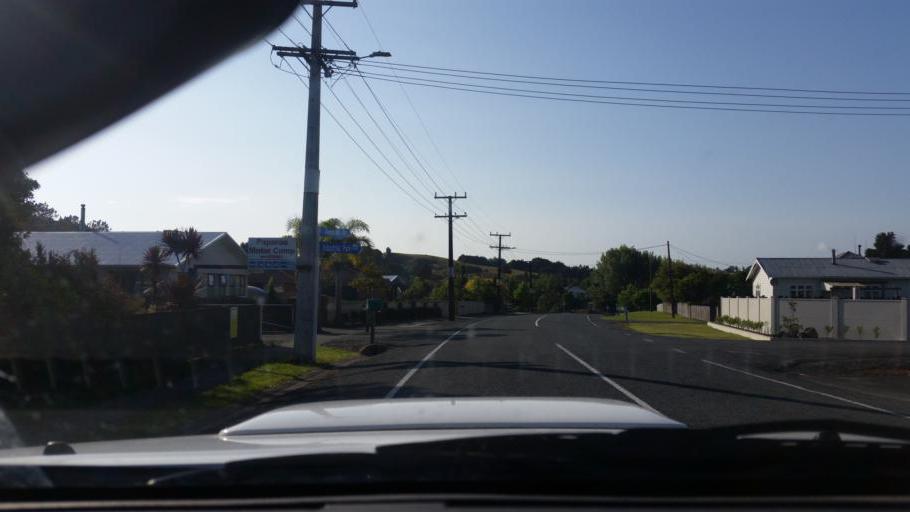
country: NZ
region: Northland
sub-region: Whangarei
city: Ruakaka
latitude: -36.1070
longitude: 174.2283
